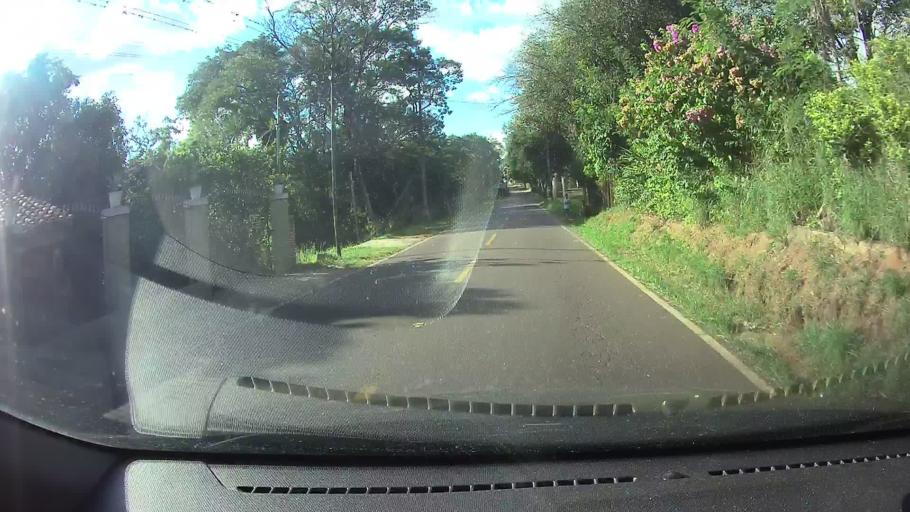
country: PY
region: Cordillera
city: Caacupe
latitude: -25.3802
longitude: -57.1963
